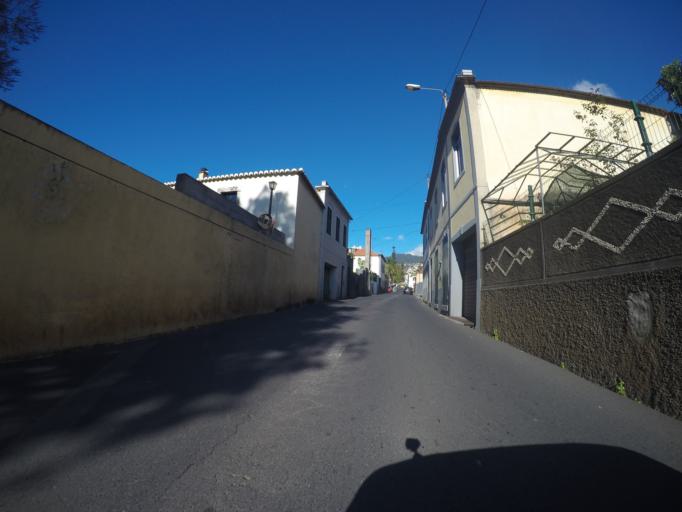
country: PT
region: Madeira
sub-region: Funchal
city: Nossa Senhora do Monte
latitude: 32.6579
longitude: -16.9285
